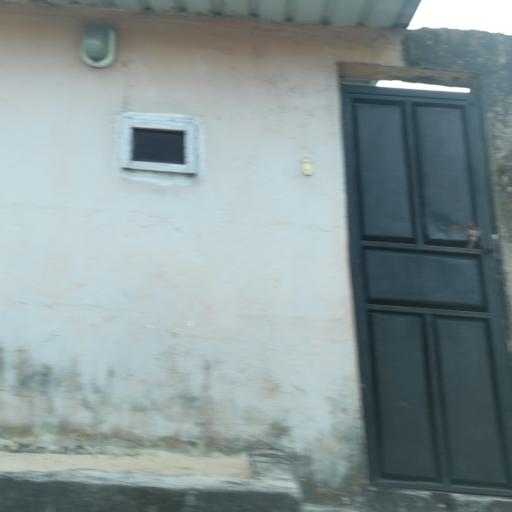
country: NG
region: Rivers
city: Port Harcourt
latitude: 4.7936
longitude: 7.0280
